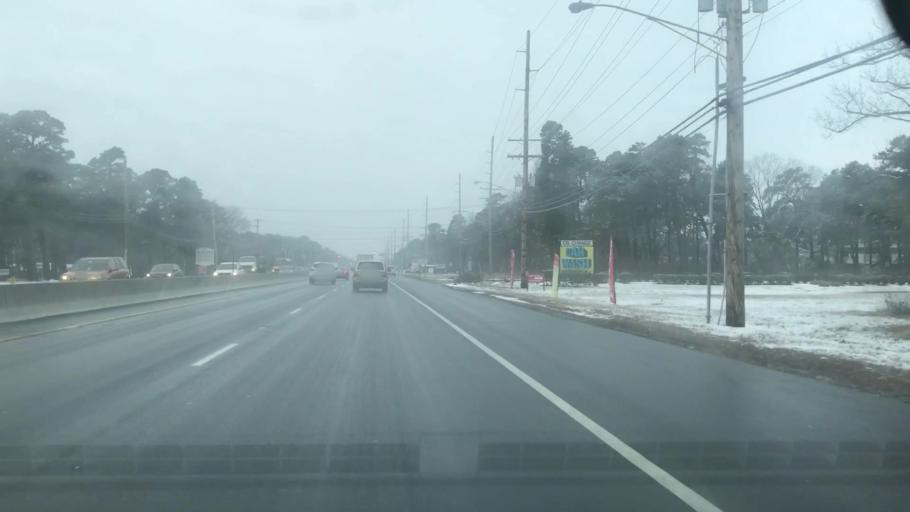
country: US
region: New Jersey
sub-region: Ocean County
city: Leisure Village
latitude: 40.0536
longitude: -74.1757
